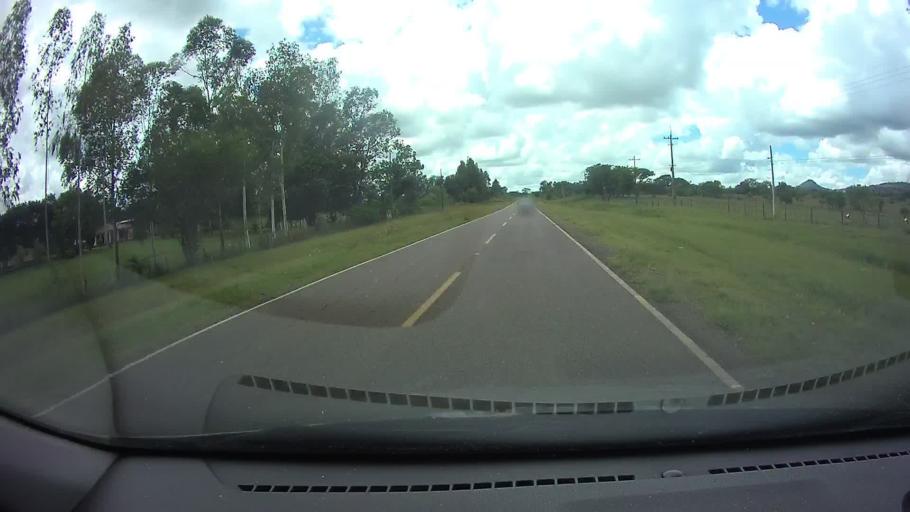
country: PY
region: Paraguari
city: La Colmena
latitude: -25.8966
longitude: -56.9563
